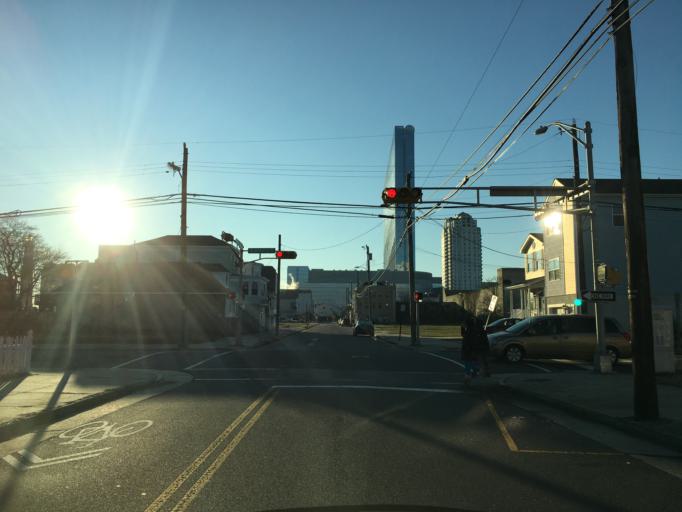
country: US
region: New Jersey
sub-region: Atlantic County
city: Atlantic City
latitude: 39.3684
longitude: -74.4180
